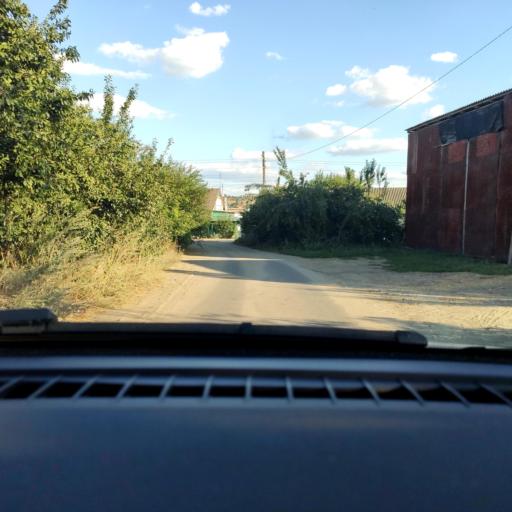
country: RU
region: Voronezj
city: Devitsa
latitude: 51.6492
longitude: 38.9587
